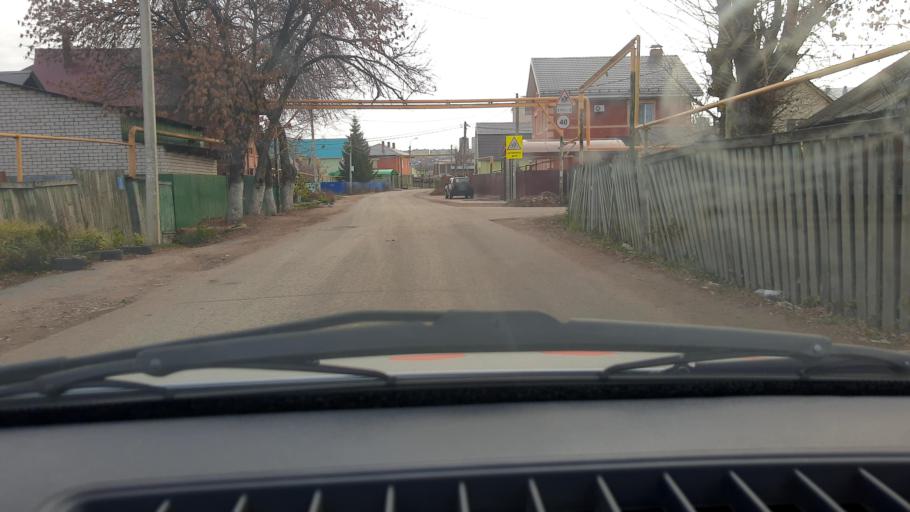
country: RU
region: Bashkortostan
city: Mikhaylovka
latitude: 54.7407
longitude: 55.9006
